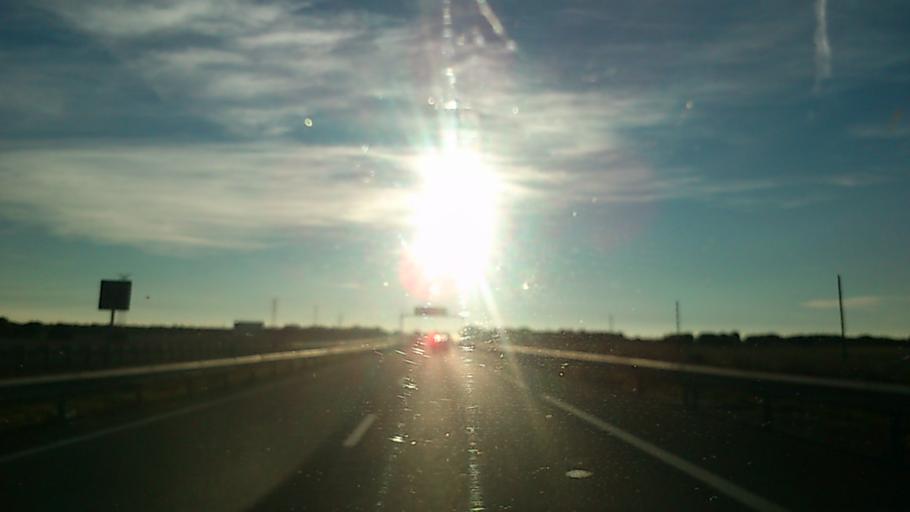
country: ES
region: Castille-La Mancha
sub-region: Provincia de Guadalajara
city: Gajanejos
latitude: 40.8341
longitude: -2.9043
